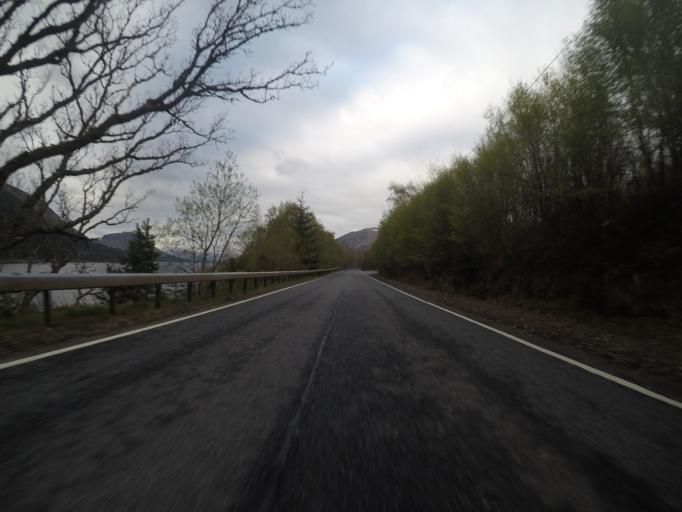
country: GB
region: Scotland
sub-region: Highland
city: Kingussie
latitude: 56.9558
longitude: -4.4785
